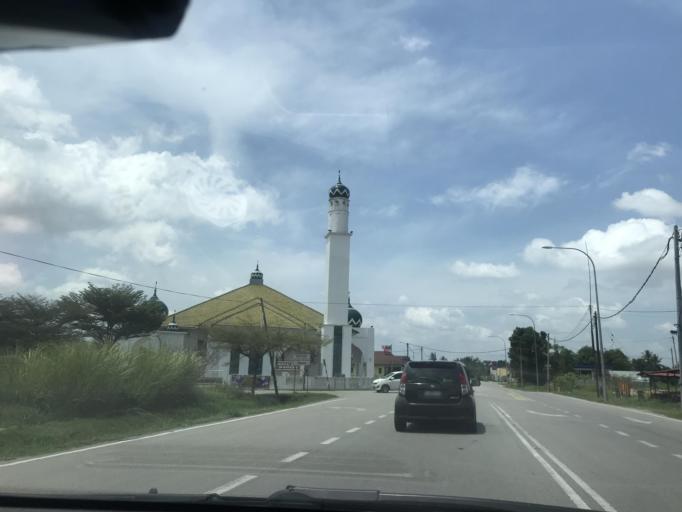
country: MY
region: Kelantan
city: Kota Bharu
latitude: 6.1565
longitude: 102.2015
